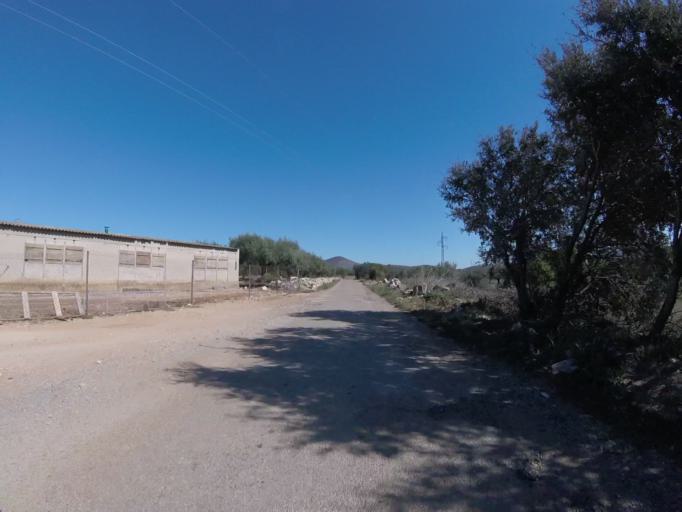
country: ES
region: Valencia
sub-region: Provincia de Castello
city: Santa Magdalena de Pulpis
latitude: 40.3525
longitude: 0.2814
